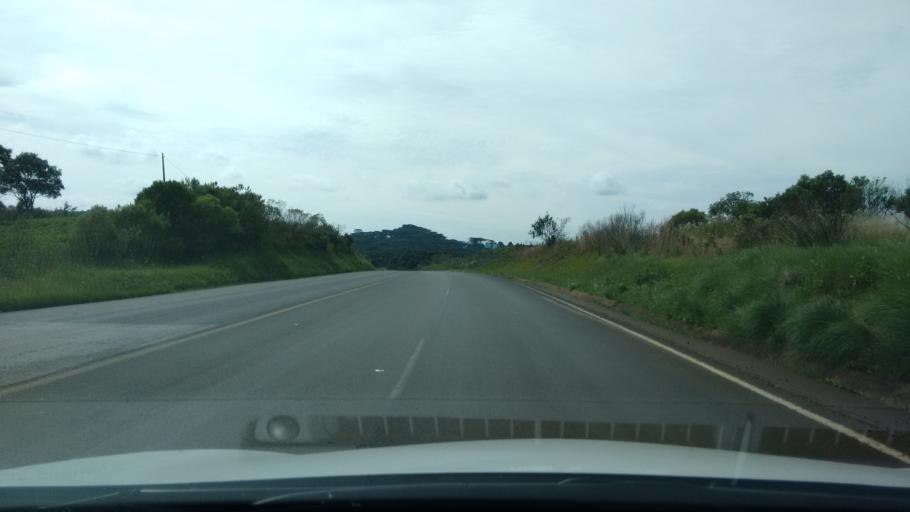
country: BR
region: Santa Catarina
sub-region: Curitibanos
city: Curitibanos
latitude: -27.3115
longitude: -50.6051
